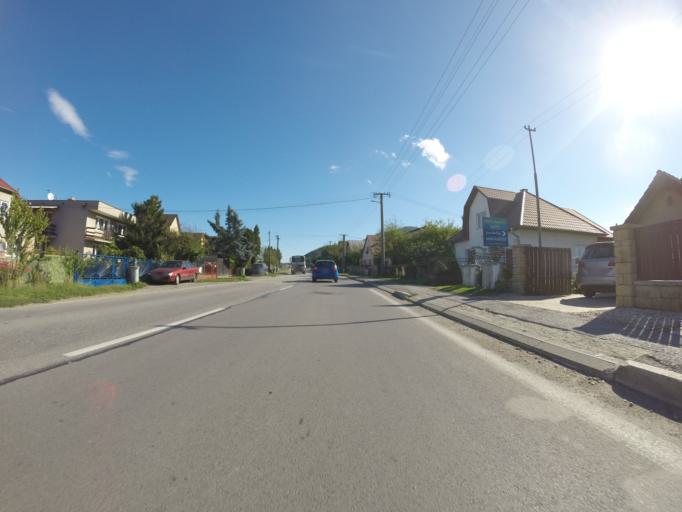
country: SK
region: Nitriansky
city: Ilava
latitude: 49.0130
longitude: 18.2677
